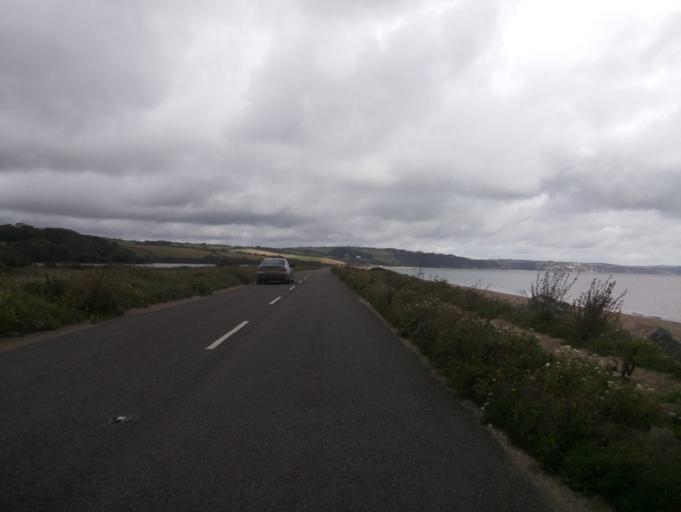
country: GB
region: England
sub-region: Devon
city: Dartmouth
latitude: 50.2750
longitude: -3.6500
